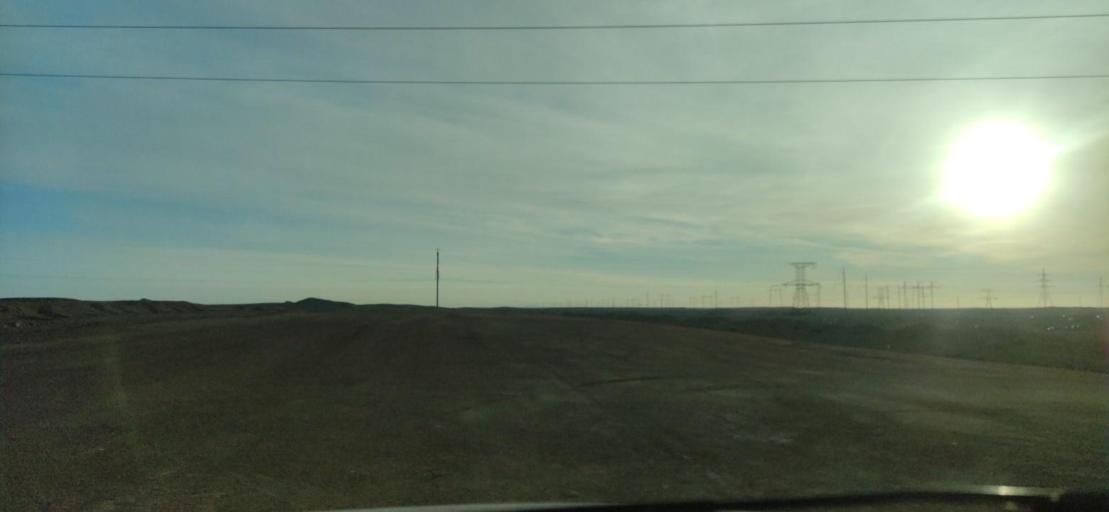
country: KZ
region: Qaraghandy
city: Saryshaghan
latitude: 46.1229
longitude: 73.5956
